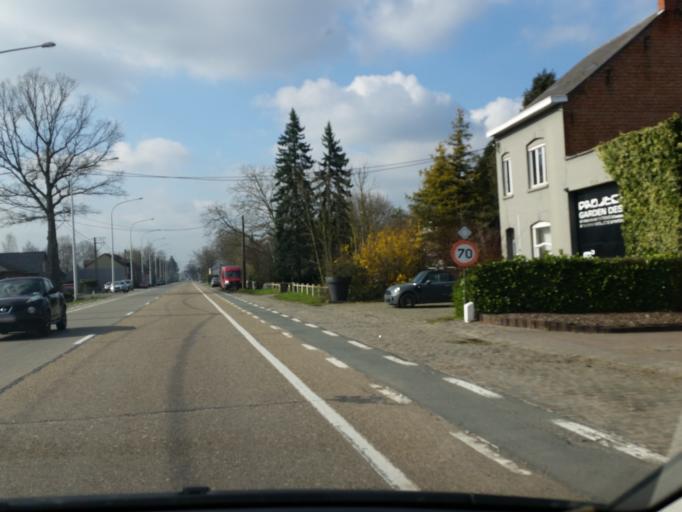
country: BE
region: Flanders
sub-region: Provincie Vlaams-Brabant
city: Herent
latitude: 50.9208
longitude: 4.6473
